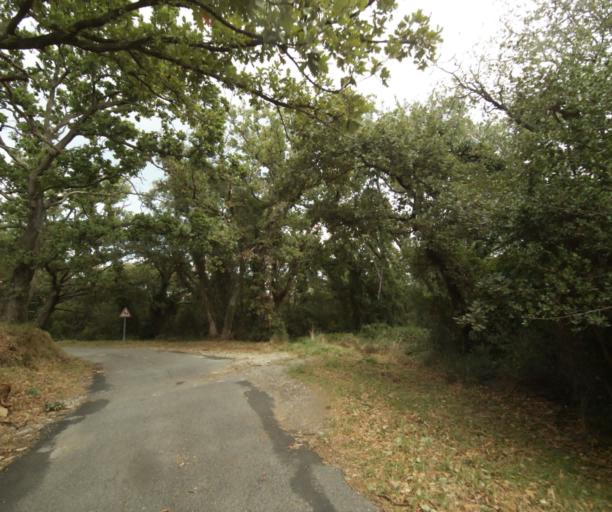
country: FR
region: Languedoc-Roussillon
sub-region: Departement des Pyrenees-Orientales
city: Argelers
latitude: 42.5317
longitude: 3.0081
